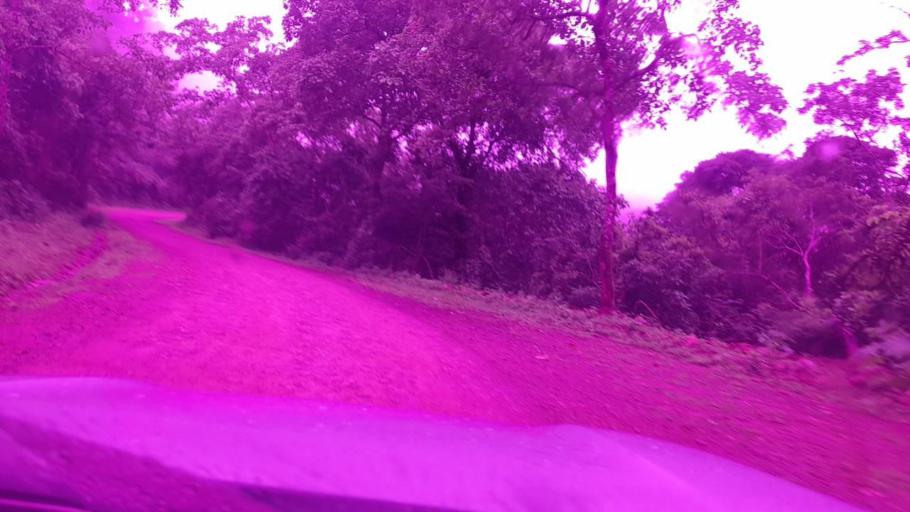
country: ET
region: Southern Nations, Nationalities, and People's Region
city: Bonga
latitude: 7.5143
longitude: 36.0591
